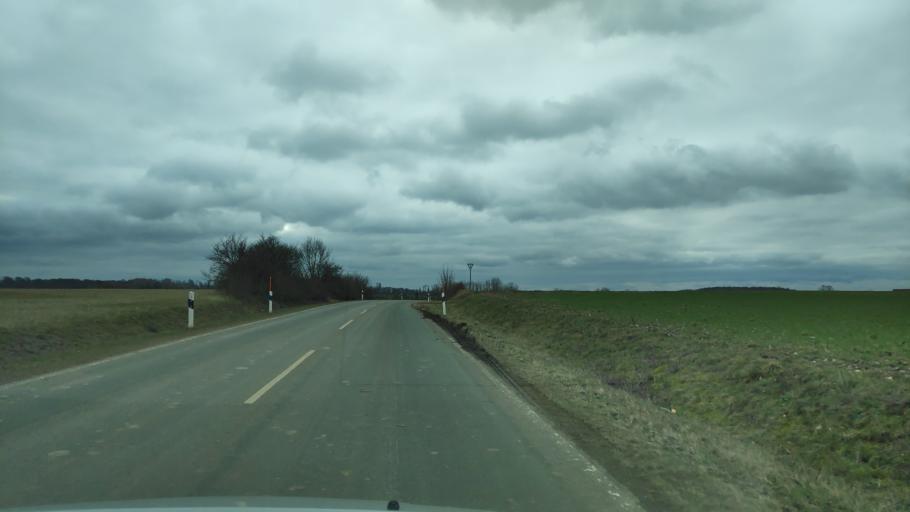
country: DE
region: Lower Saxony
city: Rehren
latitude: 52.2183
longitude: 9.2893
